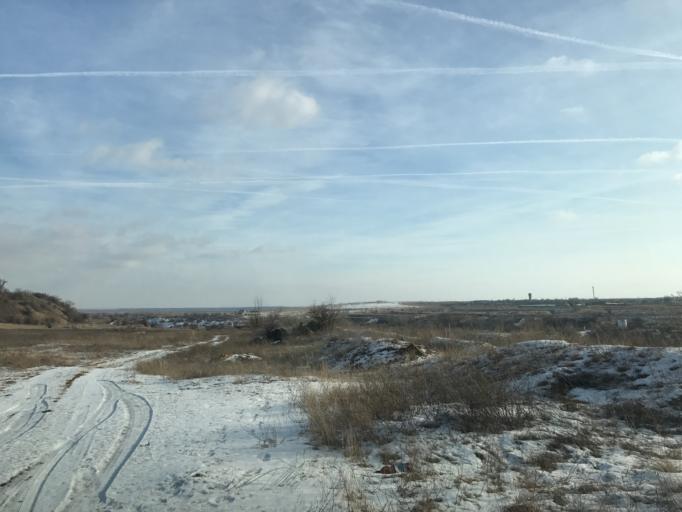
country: RU
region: Rostov
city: Staraya Stanitsa
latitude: 48.2470
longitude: 40.4007
